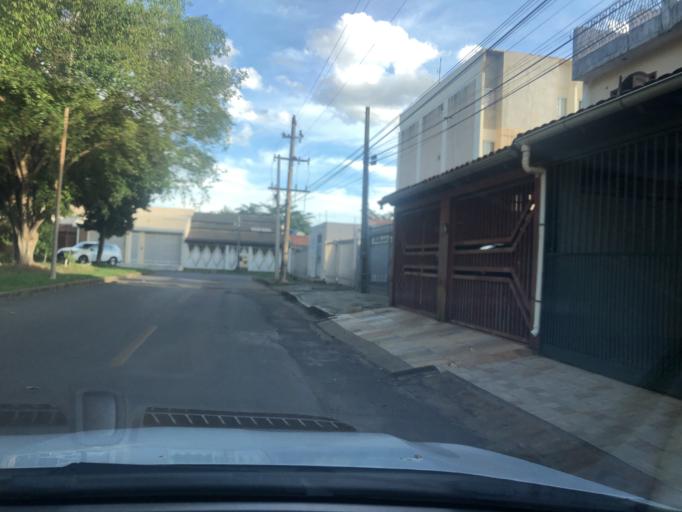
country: BR
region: Federal District
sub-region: Brasilia
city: Brasilia
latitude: -15.8242
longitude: -47.9863
